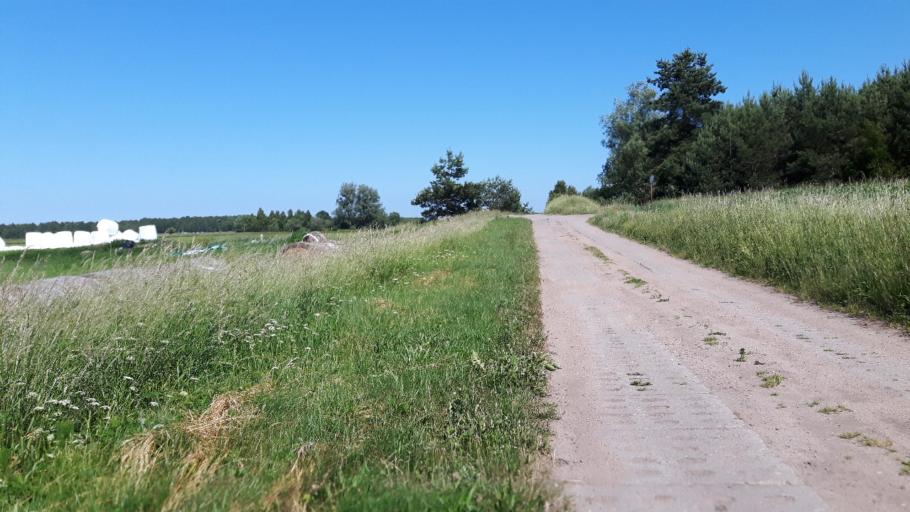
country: PL
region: Pomeranian Voivodeship
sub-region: Powiat slupski
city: Glowczyce
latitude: 54.6416
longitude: 17.3615
